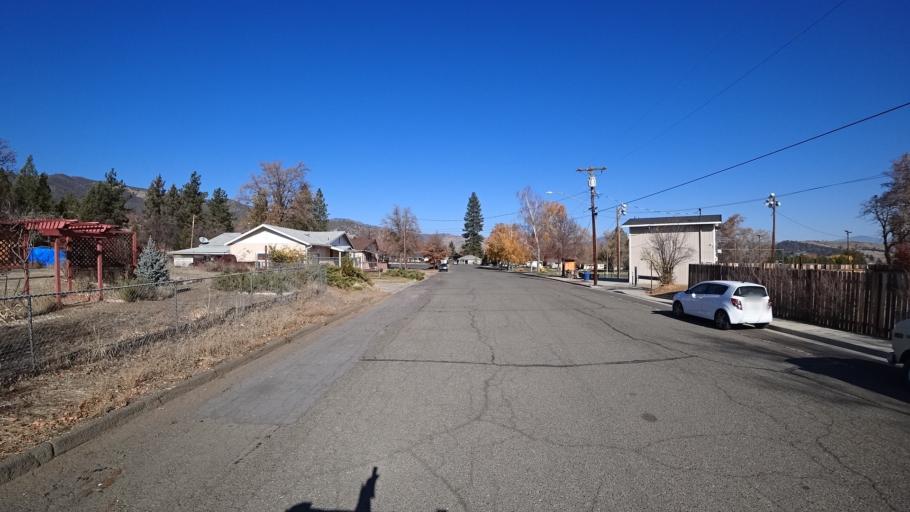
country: US
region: California
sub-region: Siskiyou County
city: Yreka
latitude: 41.7382
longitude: -122.6415
